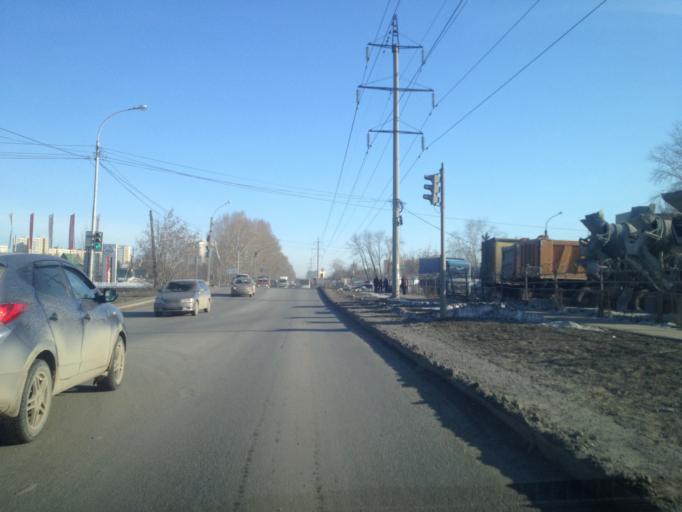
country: RU
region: Sverdlovsk
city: Sovkhoznyy
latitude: 56.7644
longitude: 60.5920
